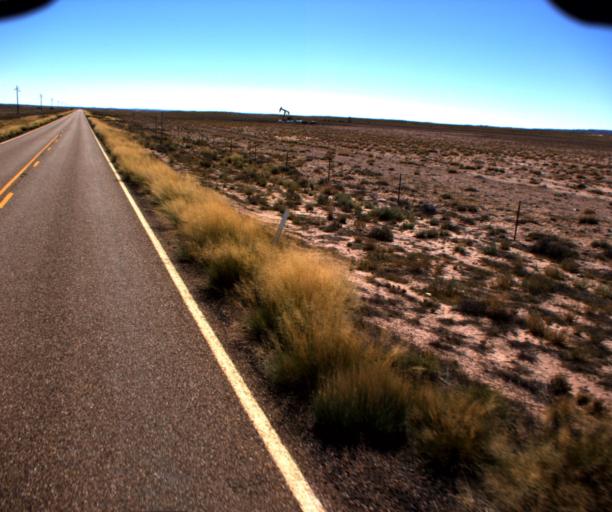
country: US
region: Arizona
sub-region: Navajo County
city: Holbrook
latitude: 35.1141
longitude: -110.0937
